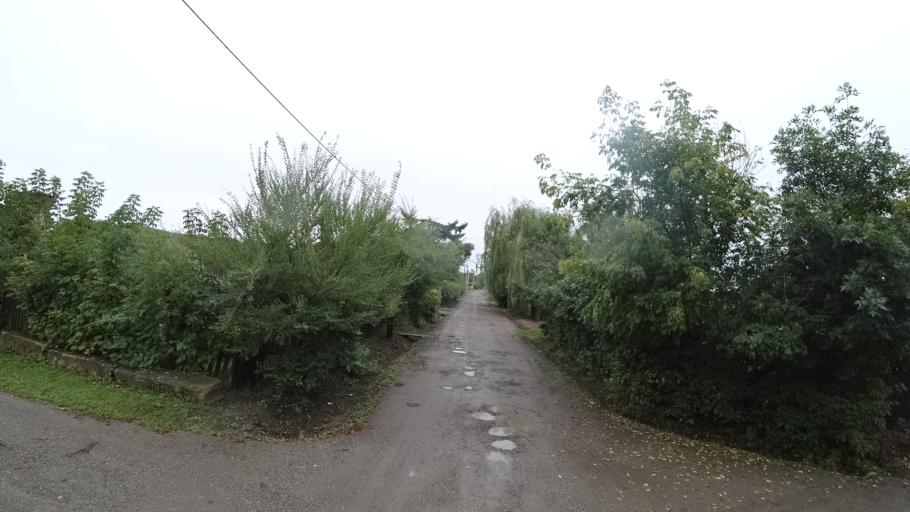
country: RU
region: Primorskiy
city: Monastyrishche
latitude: 44.2042
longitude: 132.4237
